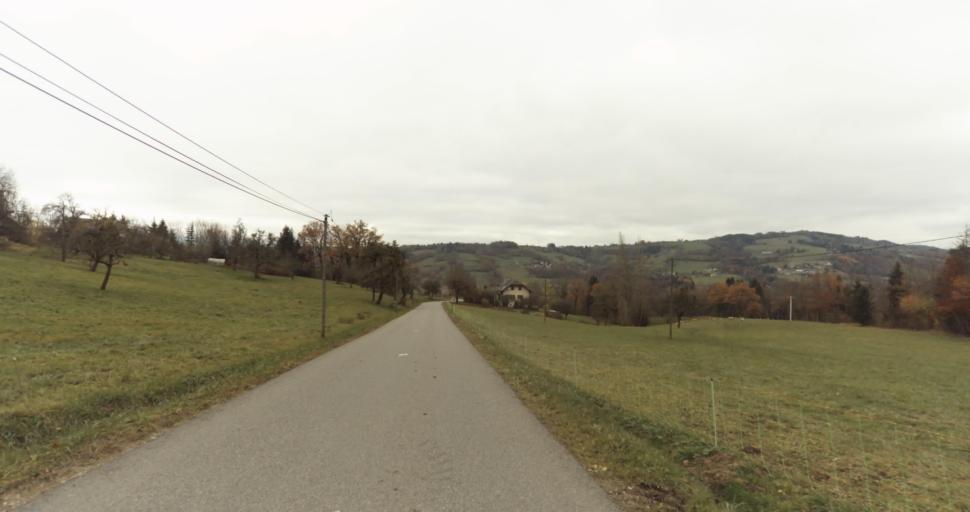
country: FR
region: Rhone-Alpes
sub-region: Departement de la Haute-Savoie
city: Thorens-Glieres
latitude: 45.9882
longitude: 6.2193
